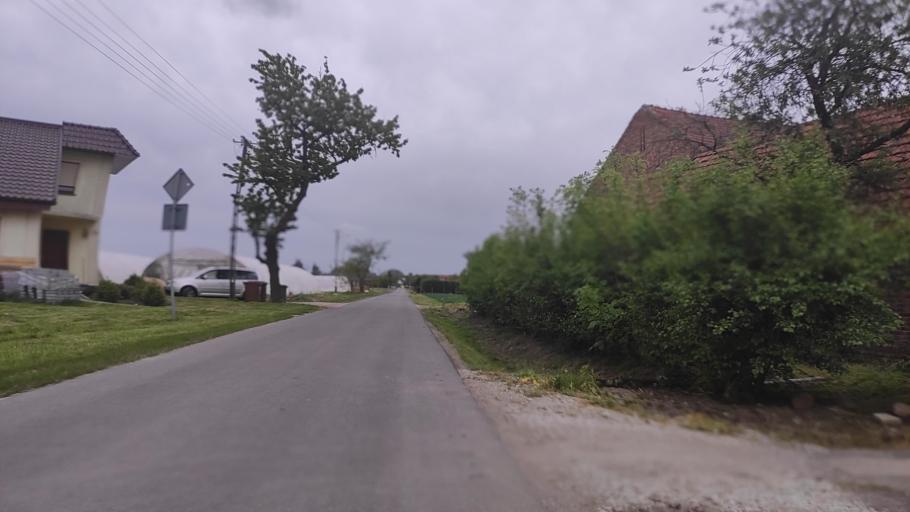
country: PL
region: Greater Poland Voivodeship
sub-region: Powiat poznanski
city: Swarzedz
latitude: 52.4113
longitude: 17.1282
